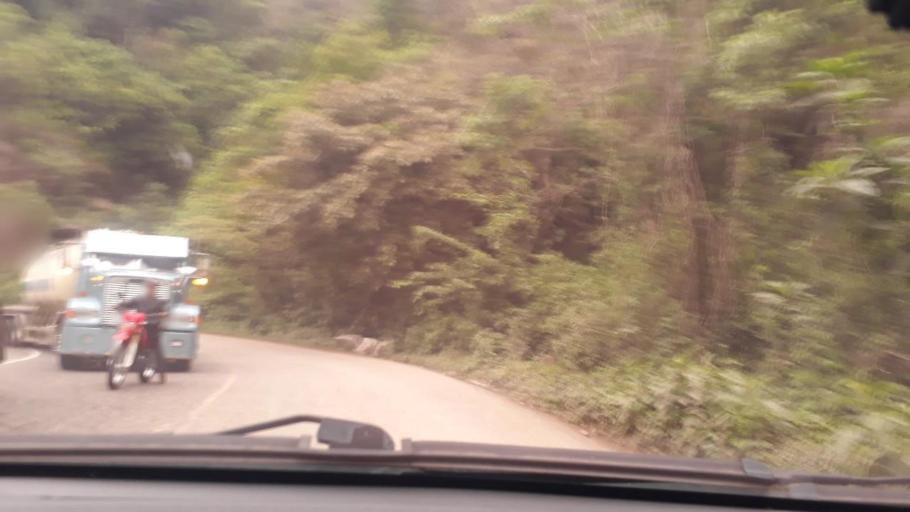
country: GT
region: El Progreso
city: Sansare
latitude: 14.7278
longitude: -90.0445
